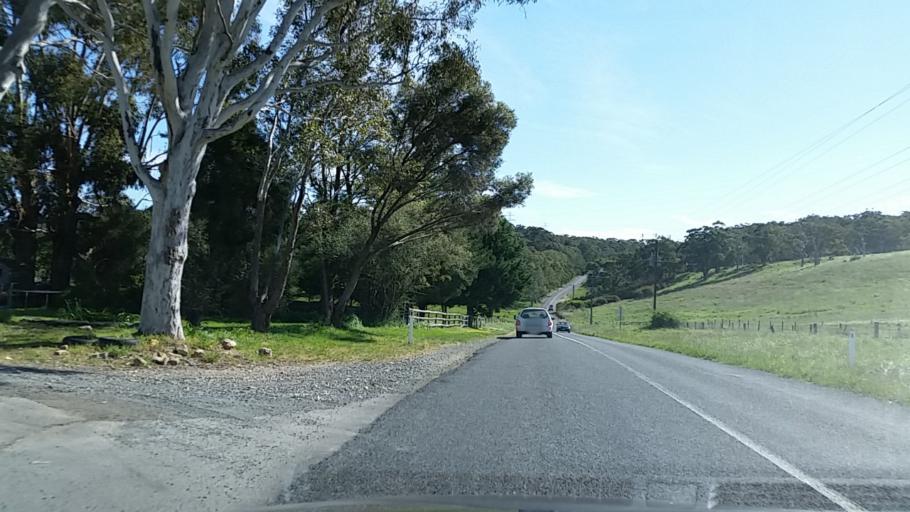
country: AU
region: South Australia
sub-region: Mount Barker
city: Little Hampton
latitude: -35.0775
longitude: 138.8336
